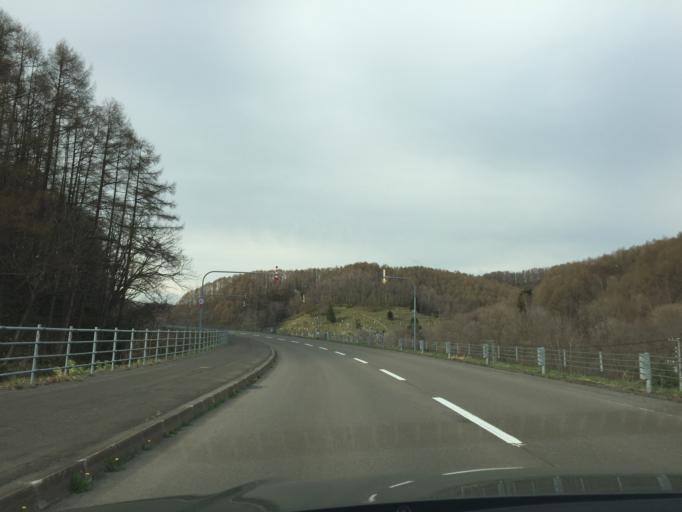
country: JP
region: Hokkaido
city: Utashinai
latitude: 43.5112
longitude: 142.0255
